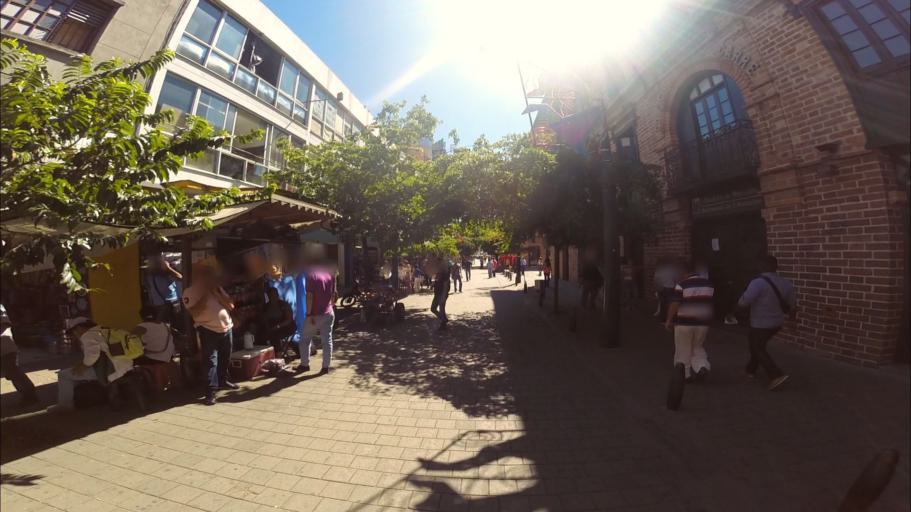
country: CO
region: Antioquia
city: Medellin
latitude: 6.2460
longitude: -75.5711
